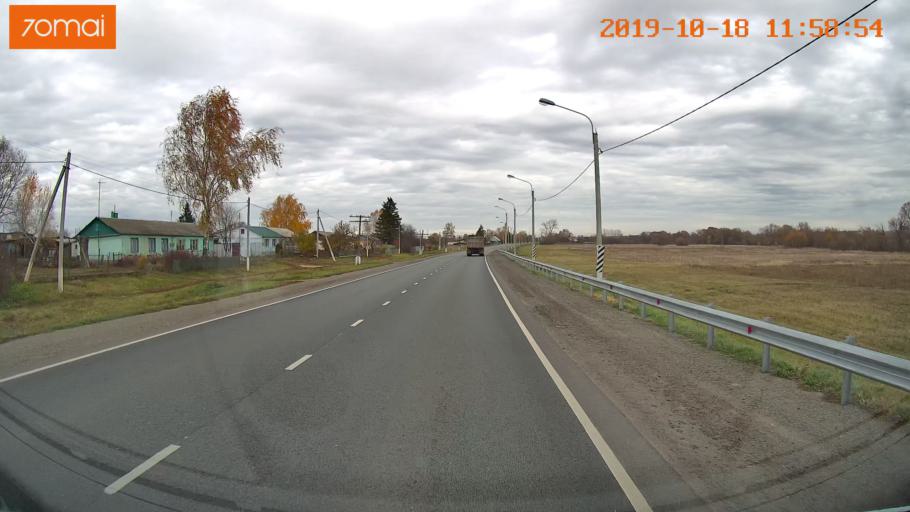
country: RU
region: Rjazan
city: Zakharovo
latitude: 54.2766
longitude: 39.1707
